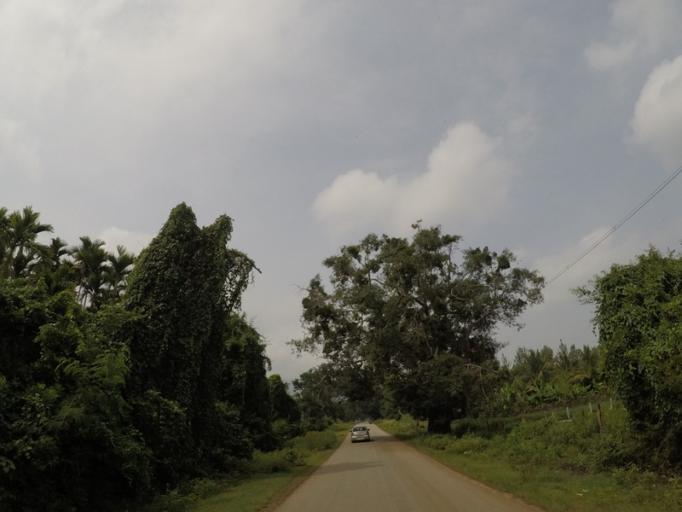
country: IN
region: Karnataka
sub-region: Chikmagalur
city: Tarikere
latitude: 13.5749
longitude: 75.8179
